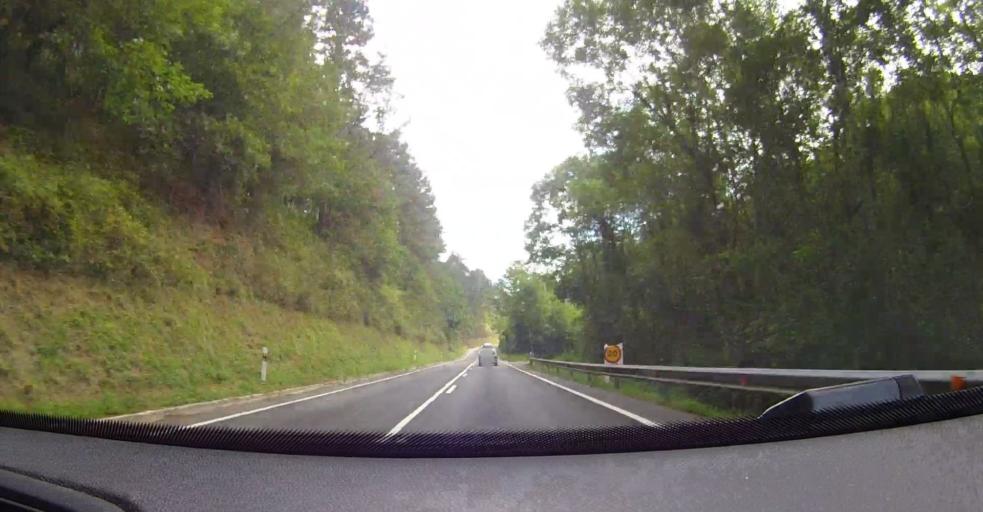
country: ES
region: Basque Country
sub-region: Bizkaia
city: Ibarrangelu
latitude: 43.3842
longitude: -2.6347
